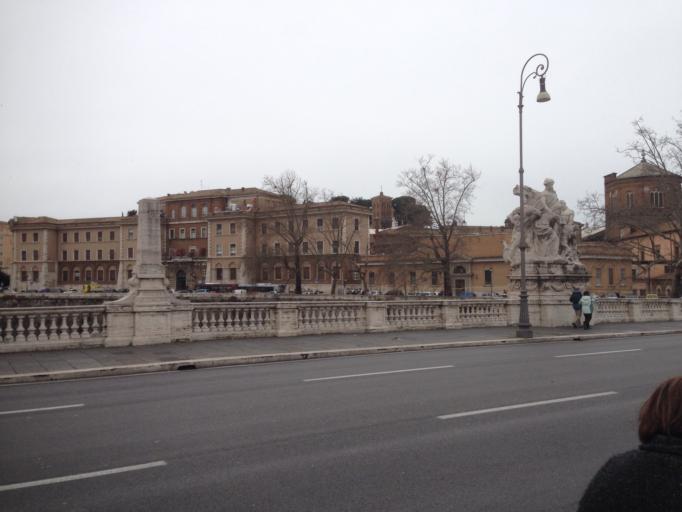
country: VA
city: Vatican City
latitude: 41.9013
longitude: 12.4644
